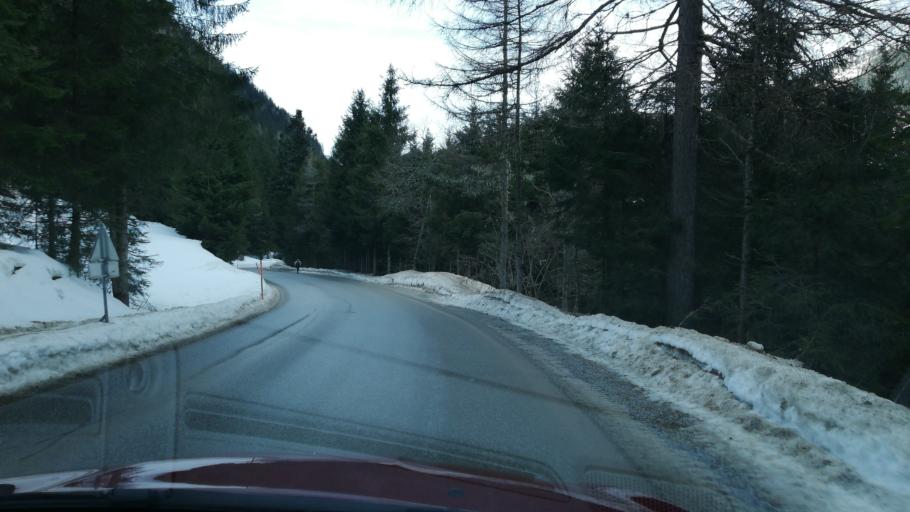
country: AT
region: Styria
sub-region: Politischer Bezirk Liezen
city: Donnersbach
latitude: 47.4209
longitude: 14.1687
